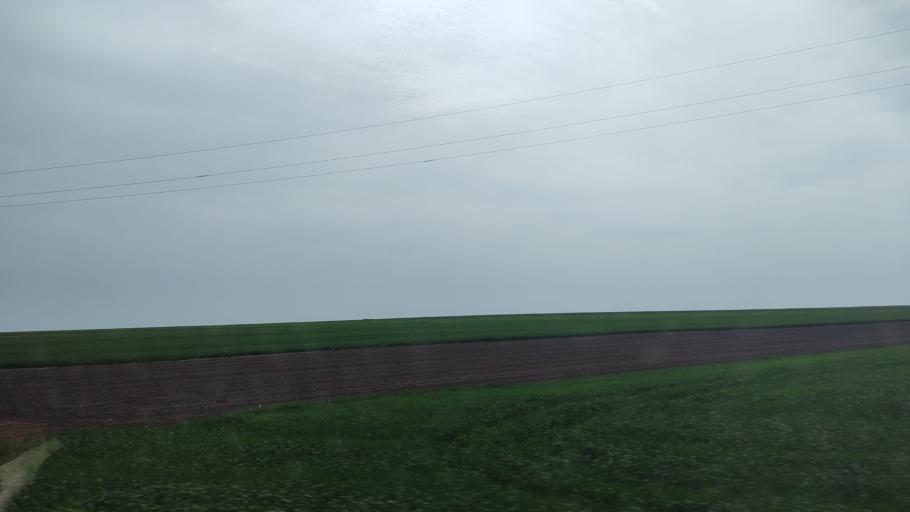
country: RO
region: Constanta
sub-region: Comuna Ciocarlia
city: Ciocarlia
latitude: 44.1087
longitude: 28.3046
